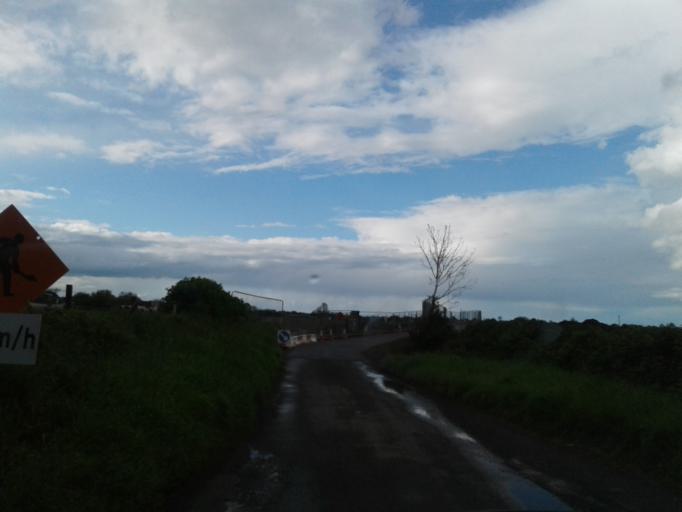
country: IE
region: Leinster
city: Ballymun
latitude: 53.4342
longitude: -6.2903
